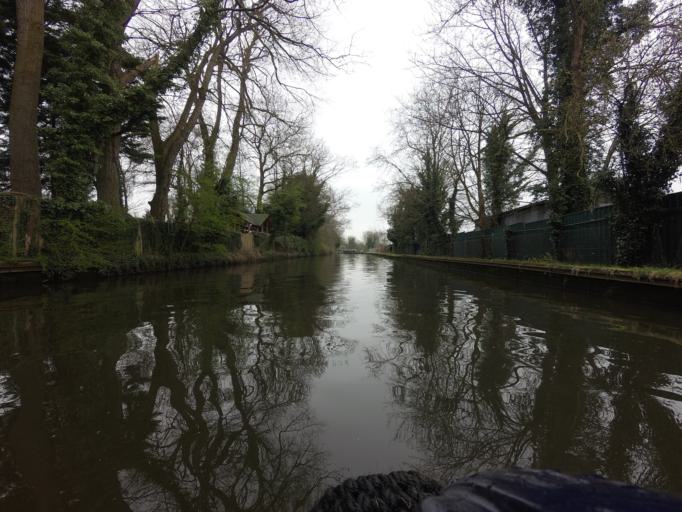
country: GB
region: England
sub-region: Hertfordshire
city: Abbots Langley
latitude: 51.6899
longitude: -0.4346
